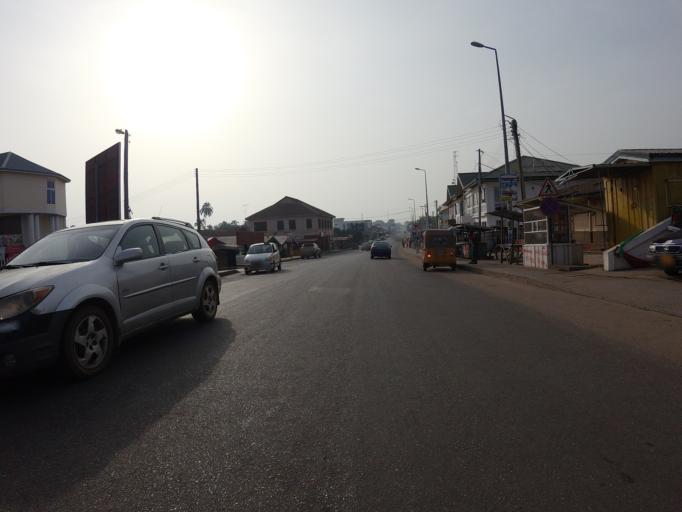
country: GH
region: Volta
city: Ho
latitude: 6.6142
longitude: 0.4689
